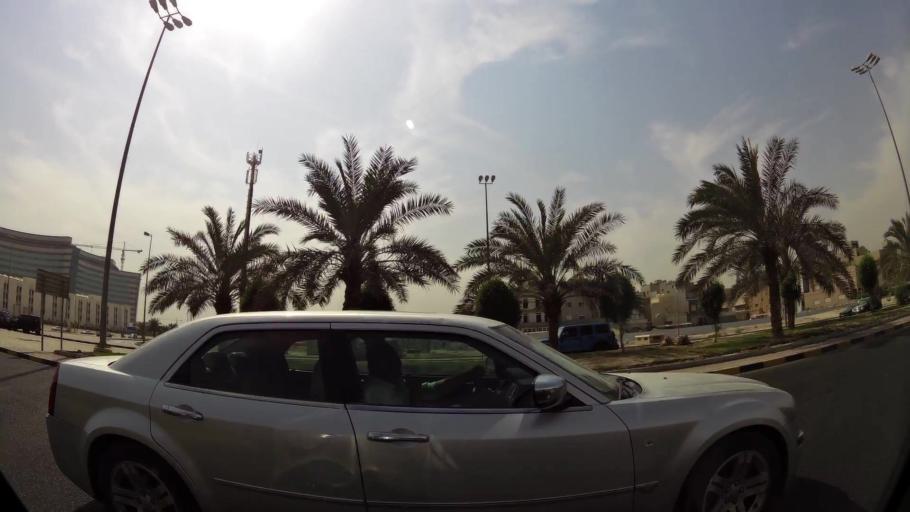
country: KW
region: Al Farwaniyah
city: Janub as Surrah
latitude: 29.2807
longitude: 48.0135
